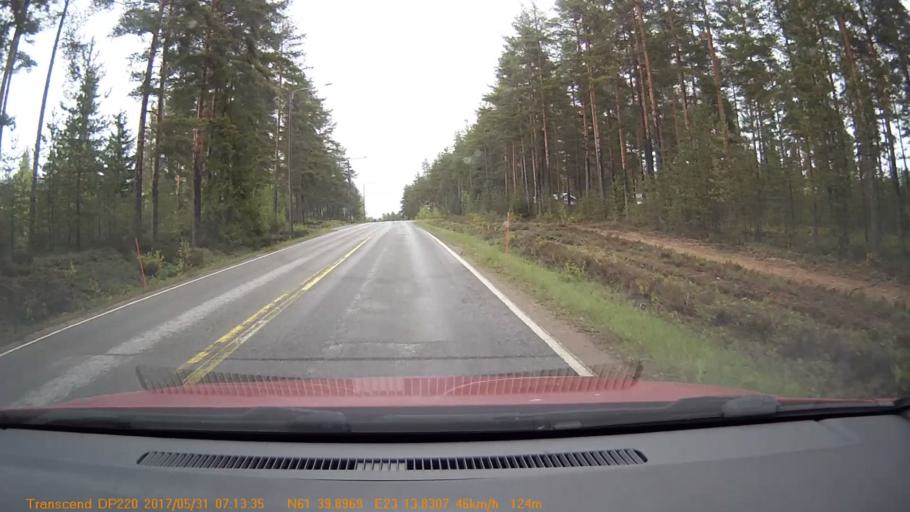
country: FI
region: Pirkanmaa
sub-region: Tampere
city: Haemeenkyroe
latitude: 61.6649
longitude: 23.2305
